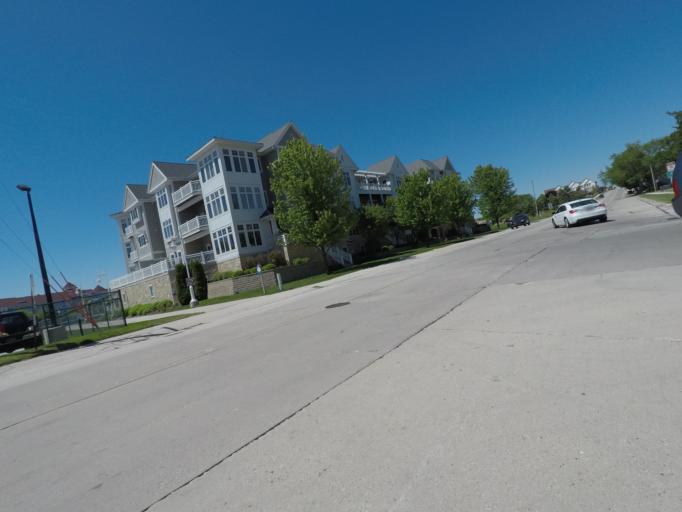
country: US
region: Wisconsin
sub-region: Sheboygan County
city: Sheboygan
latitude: 43.7498
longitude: -87.7046
